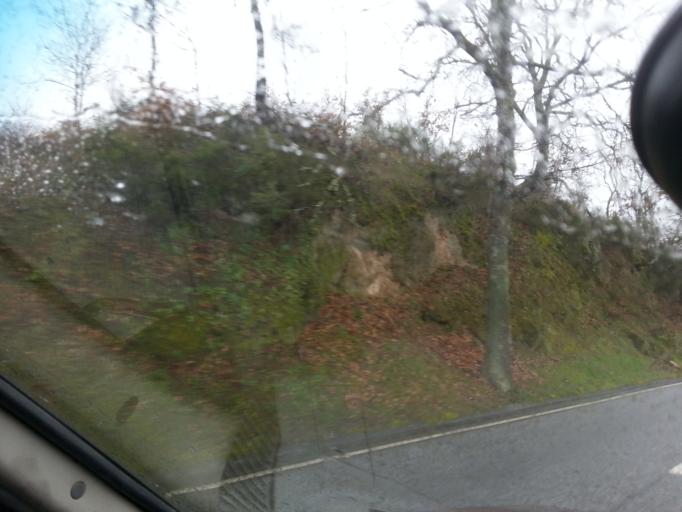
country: PT
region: Viseu
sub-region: Viseu
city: Rio de Loba
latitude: 40.6392
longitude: -7.8402
